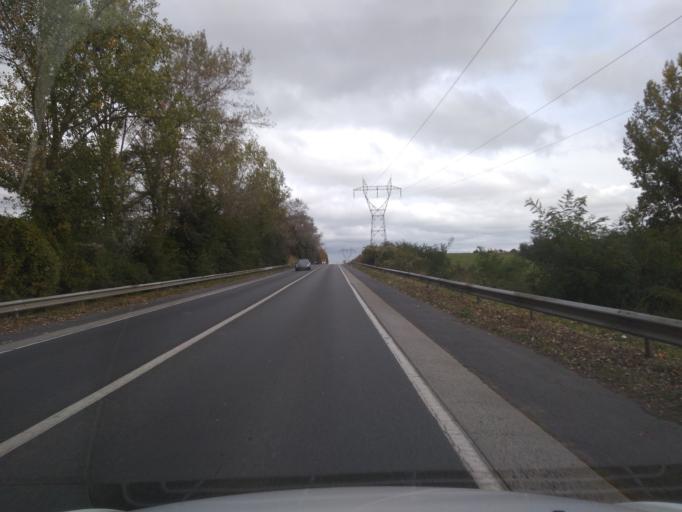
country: FR
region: Nord-Pas-de-Calais
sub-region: Departement du Nord
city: Saint-Saulve
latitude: 50.3573
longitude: 3.5613
